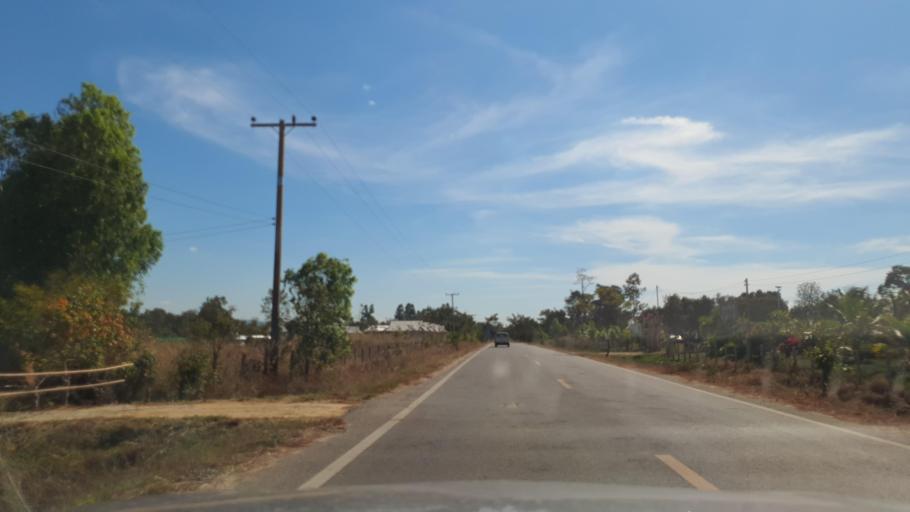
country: TH
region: Kalasin
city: Khao Wong
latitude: 16.7071
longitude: 104.1141
